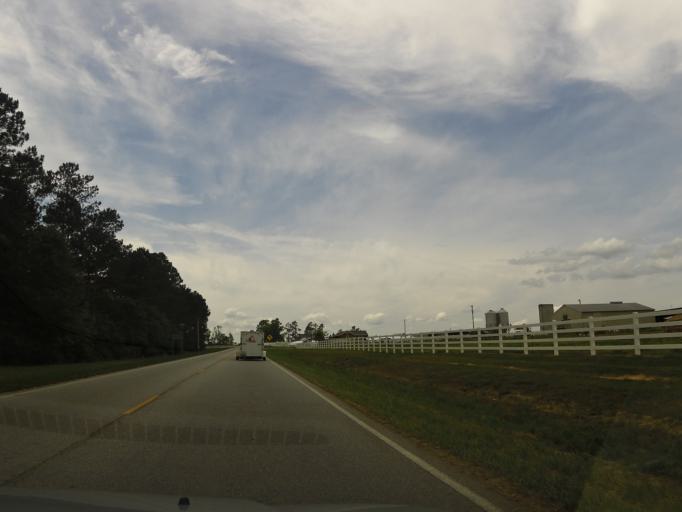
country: US
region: Georgia
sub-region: Emanuel County
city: Swainsboro
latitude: 32.5235
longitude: -82.2961
